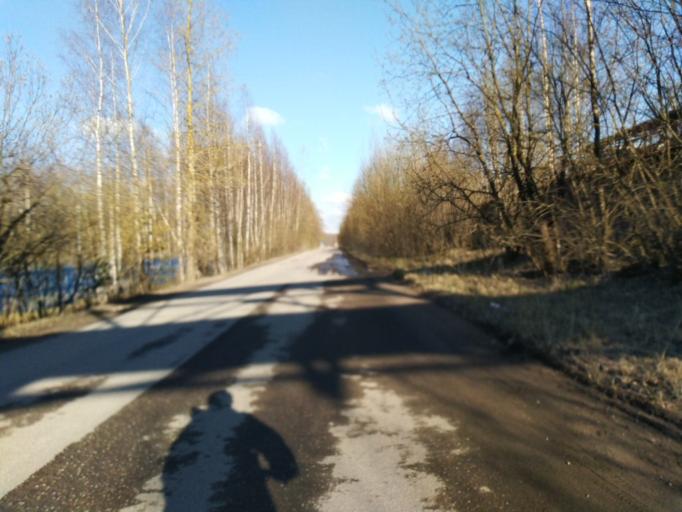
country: RU
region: Leningrad
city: Novoye Devyatkino
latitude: 60.0673
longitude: 30.4848
